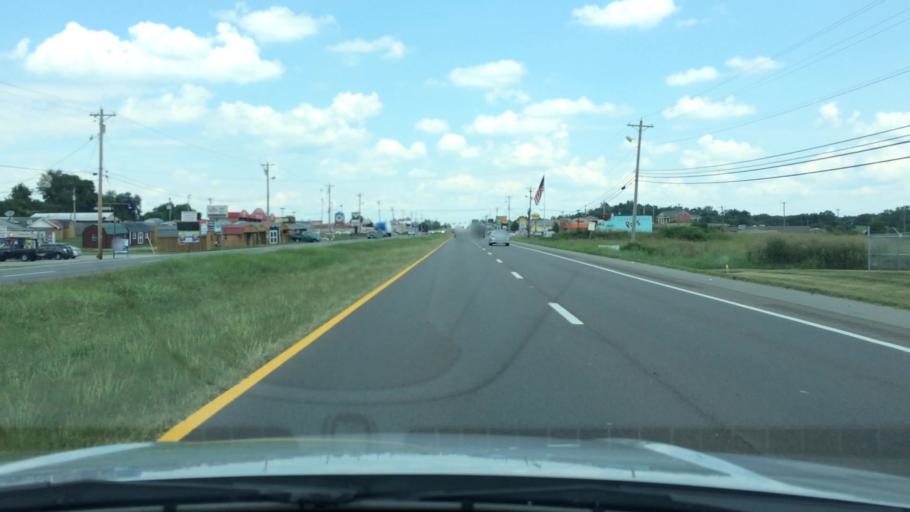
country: US
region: Tennessee
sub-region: Jefferson County
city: Jefferson City
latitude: 36.1230
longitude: -83.4736
